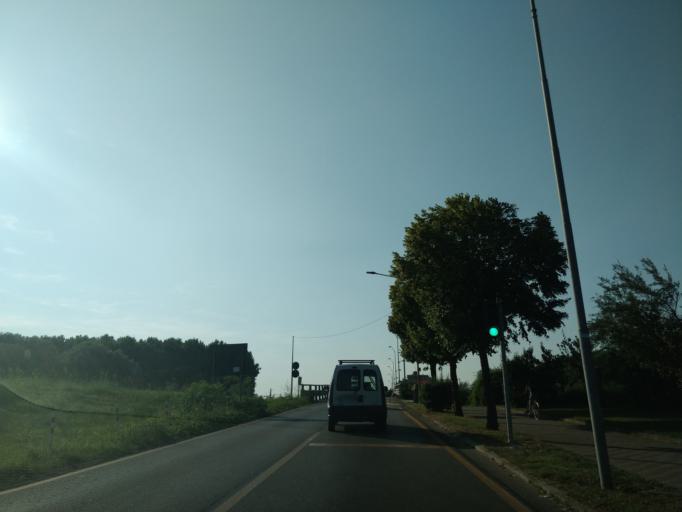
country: IT
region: Emilia-Romagna
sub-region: Provincia di Bologna
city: Pieve di Cento
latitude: 44.7203
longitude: 11.2969
